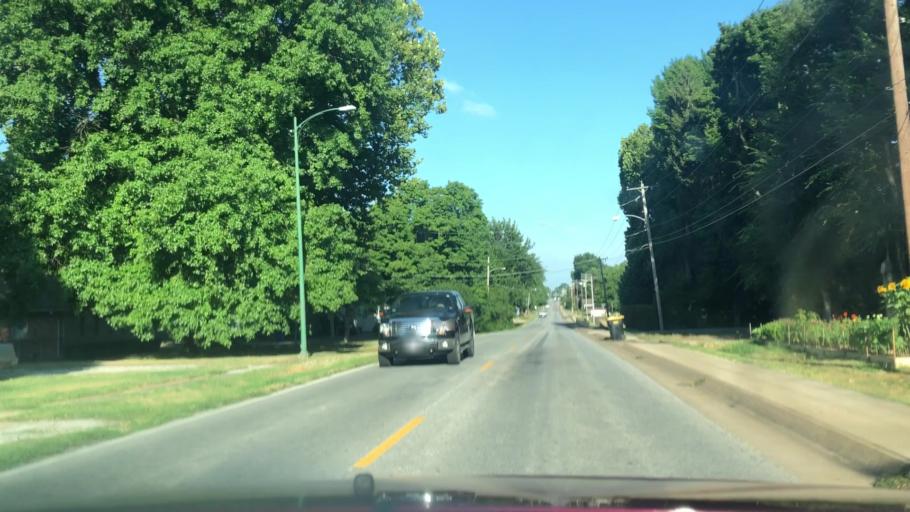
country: US
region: Missouri
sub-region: Greene County
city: Springfield
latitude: 37.1738
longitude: -93.2509
